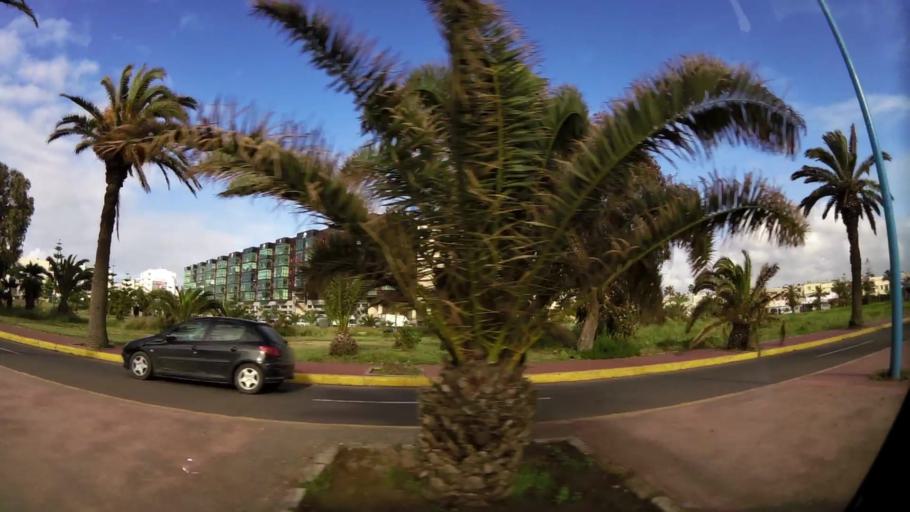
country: MA
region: Grand Casablanca
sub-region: Mohammedia
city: Mohammedia
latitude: 33.7024
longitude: -7.4008
